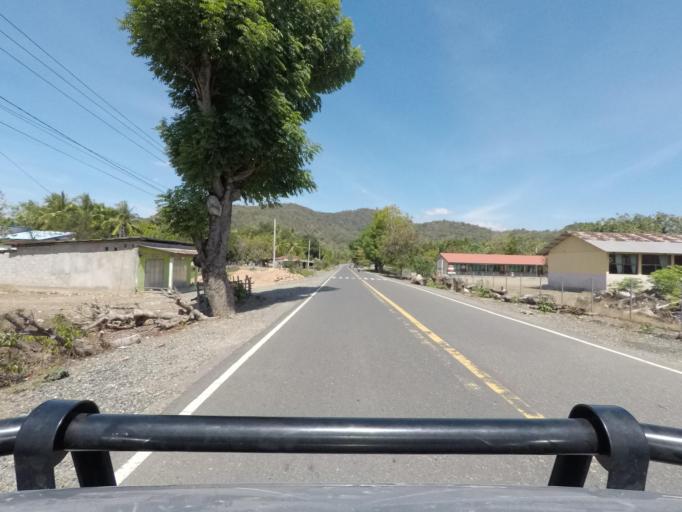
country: TL
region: Liquica
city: Maubara
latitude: -8.7923
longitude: 125.1015
